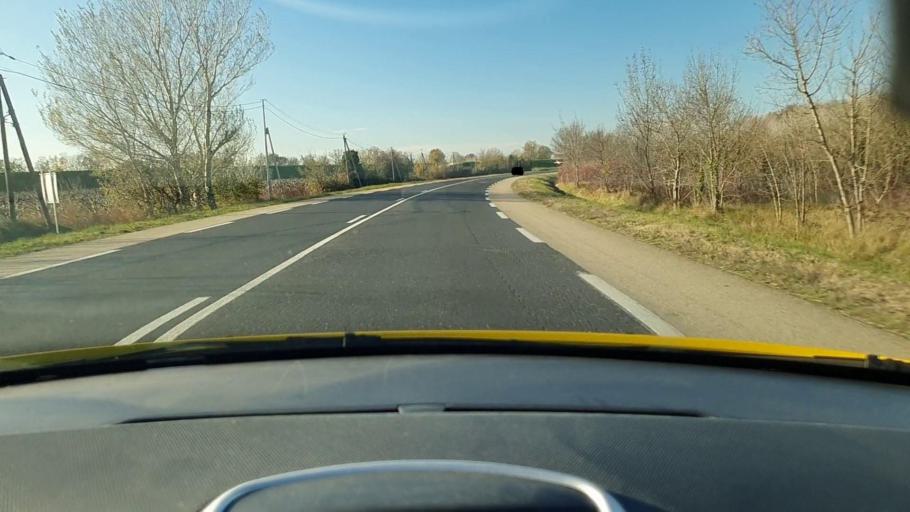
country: FR
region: Languedoc-Roussillon
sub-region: Departement du Gard
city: Fourques
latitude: 43.6946
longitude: 4.5916
